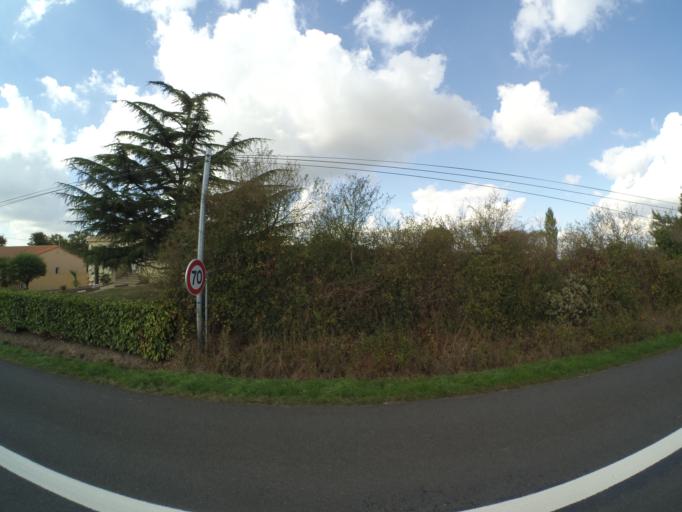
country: FR
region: Pays de la Loire
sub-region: Departement de la Loire-Atlantique
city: Remouille
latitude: 47.0640
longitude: -1.3566
